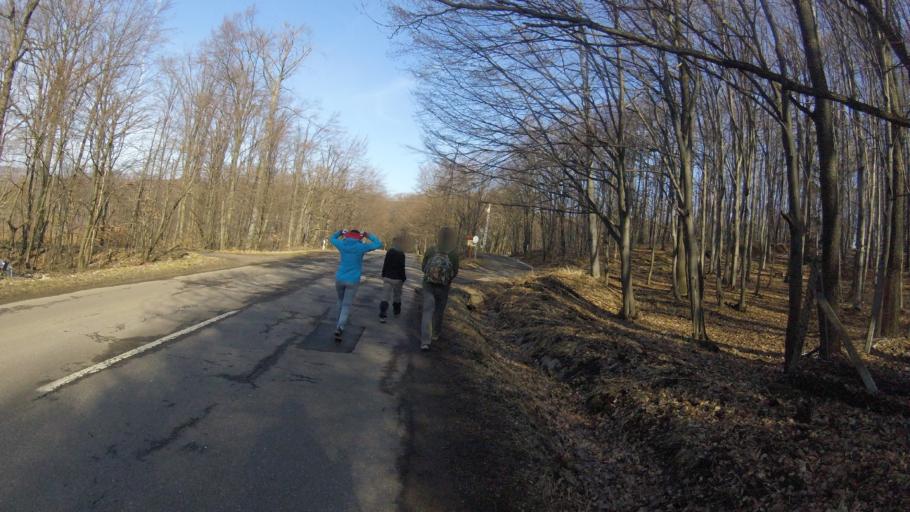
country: HU
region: Heves
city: Paradsasvar
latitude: 47.8832
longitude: 19.9774
